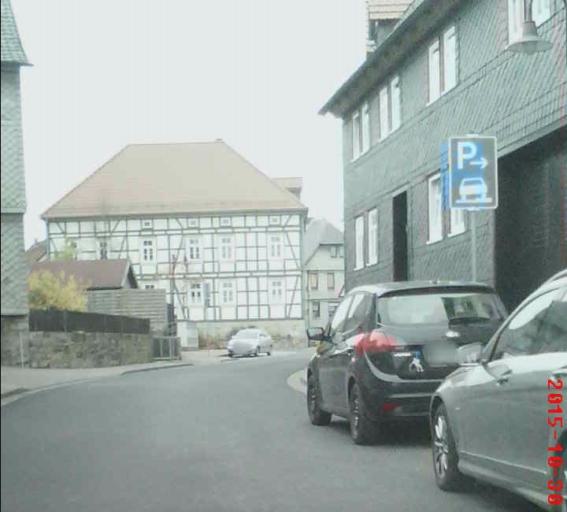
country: DE
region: Thuringia
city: Kullstedt
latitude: 51.2753
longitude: 10.2799
